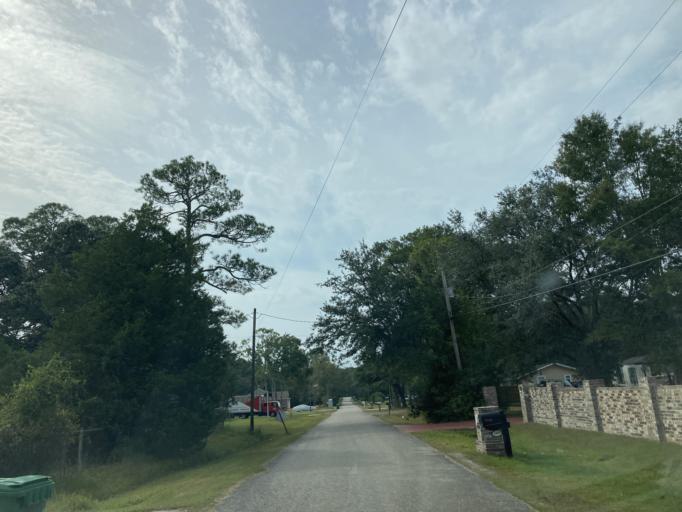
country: US
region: Mississippi
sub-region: Jackson County
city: Gulf Hills
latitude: 30.4716
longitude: -88.8434
